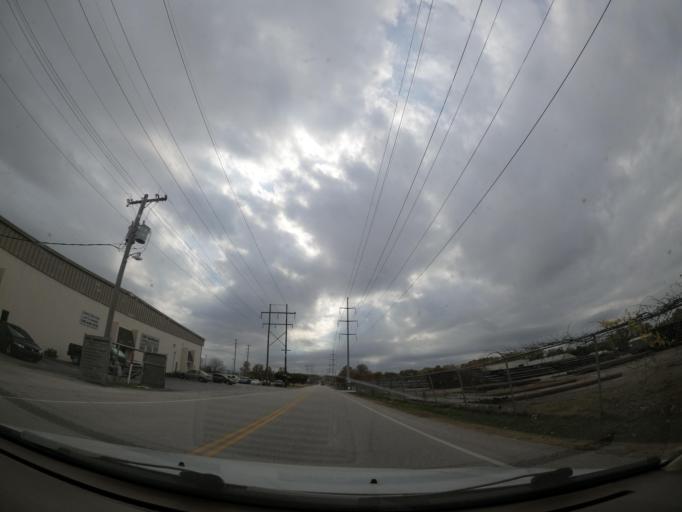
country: US
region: Oklahoma
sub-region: Tulsa County
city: Tulsa
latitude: 36.0996
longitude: -95.9936
